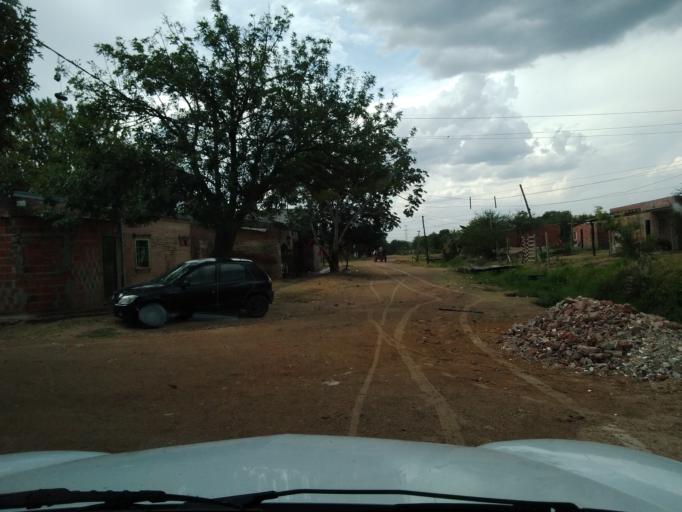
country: AR
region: Corrientes
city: Corrientes
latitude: -27.5203
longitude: -58.7878
